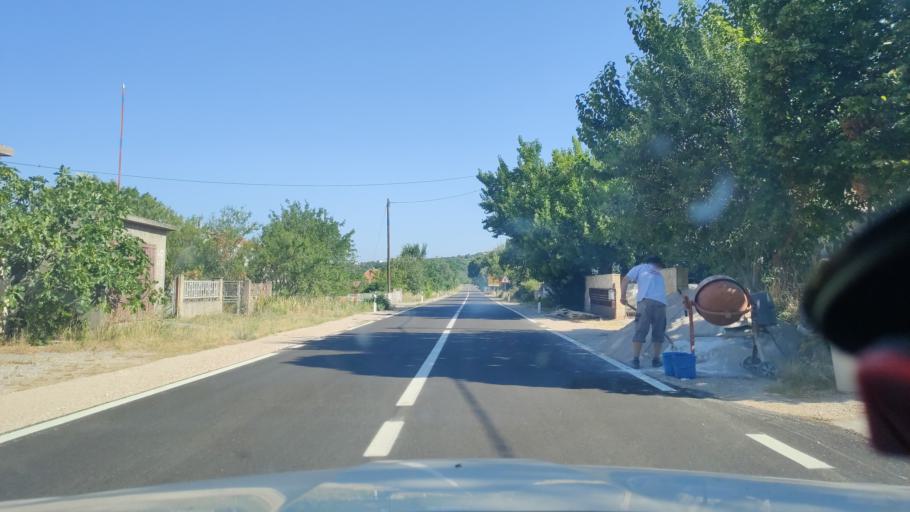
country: HR
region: Sibensko-Kniniska
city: Zaton
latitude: 43.8961
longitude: 15.8646
